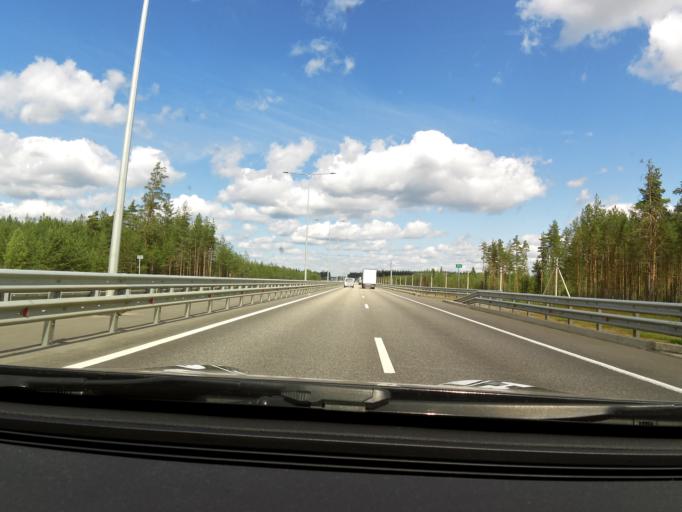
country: RU
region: Tverskaya
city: Krasnomayskiy
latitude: 57.5467
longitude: 34.2706
